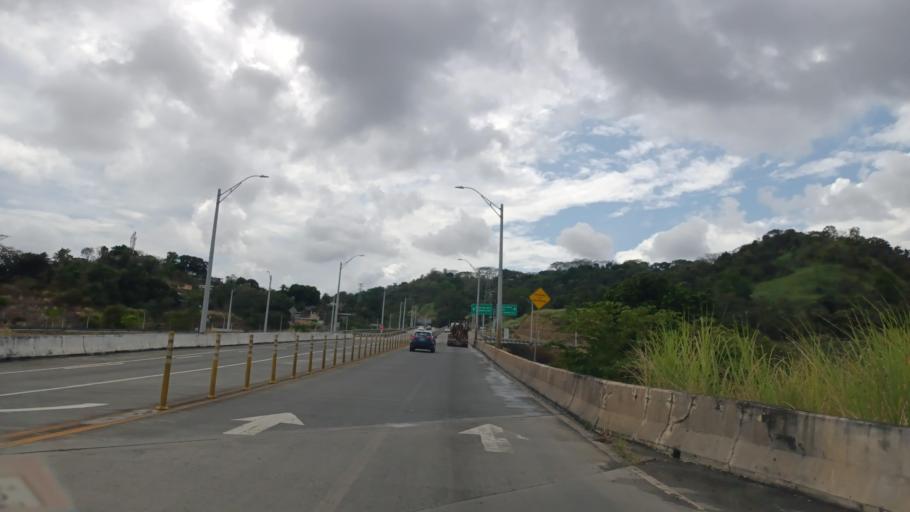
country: PA
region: Panama
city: San Miguelito
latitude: 9.0837
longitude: -79.4605
